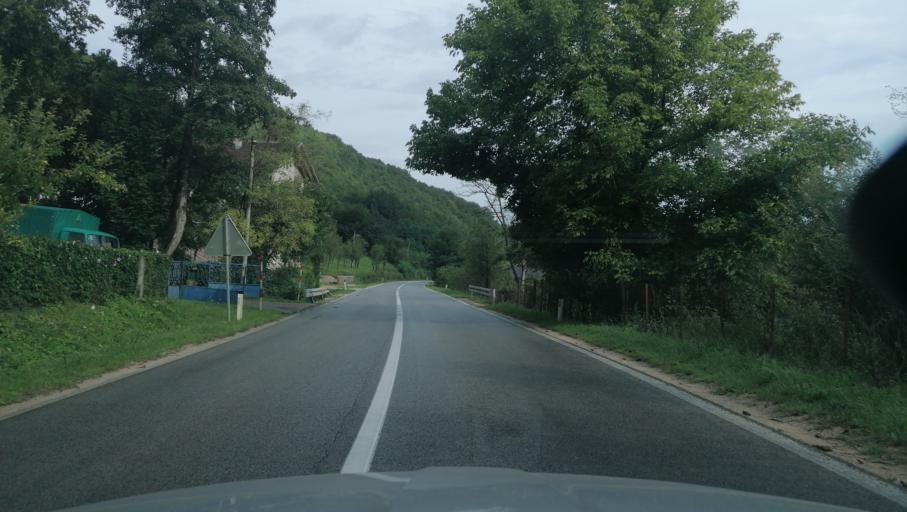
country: BA
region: Republika Srpska
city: Hiseti
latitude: 44.6460
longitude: 17.1466
